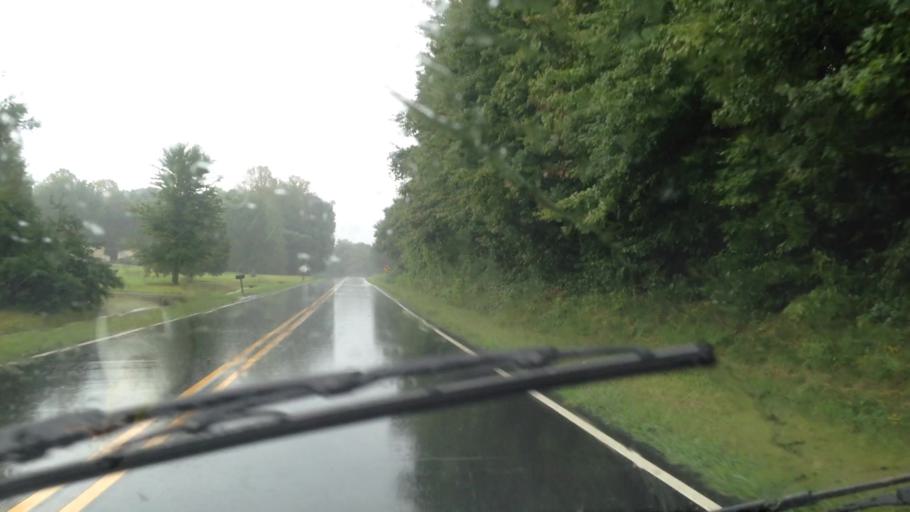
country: US
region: North Carolina
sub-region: Stokes County
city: Danbury
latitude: 36.4317
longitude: -80.1010
